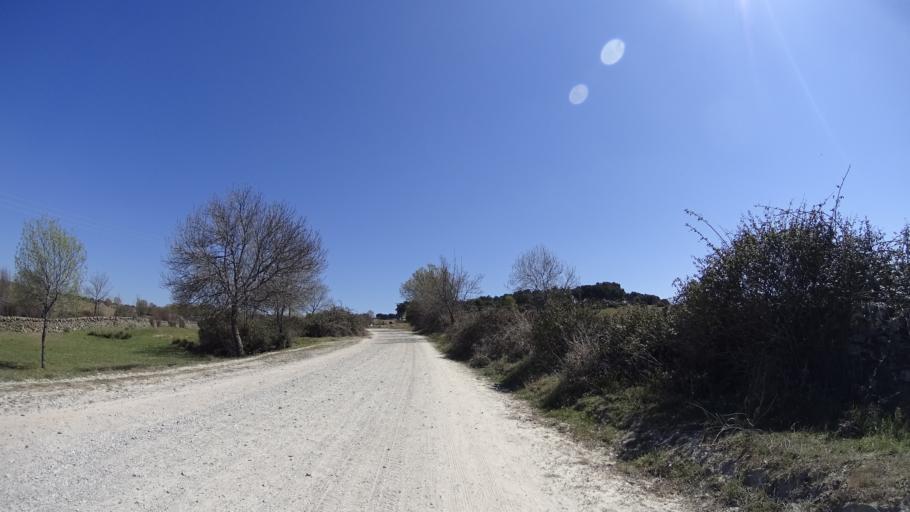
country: ES
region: Madrid
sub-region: Provincia de Madrid
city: Colmenar Viejo
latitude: 40.7041
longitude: -3.7732
